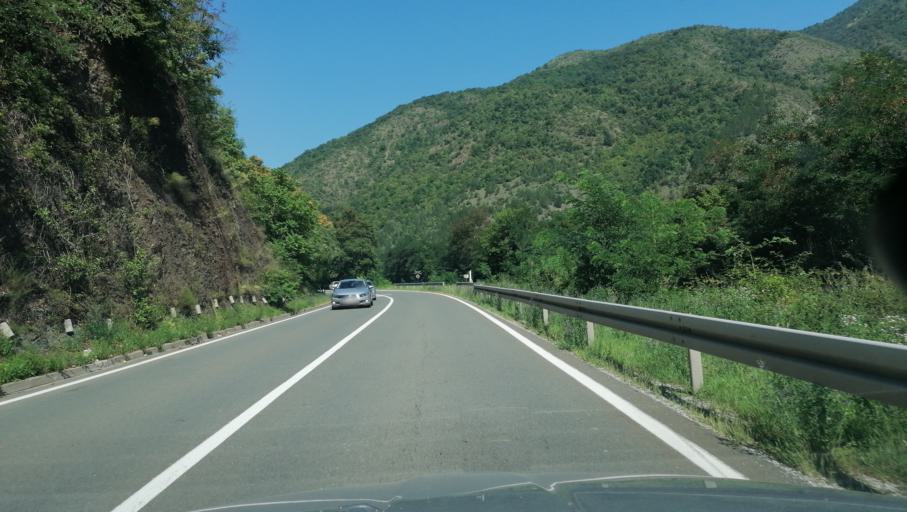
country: RS
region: Central Serbia
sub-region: Raski Okrug
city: Kraljevo
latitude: 43.6349
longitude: 20.5481
